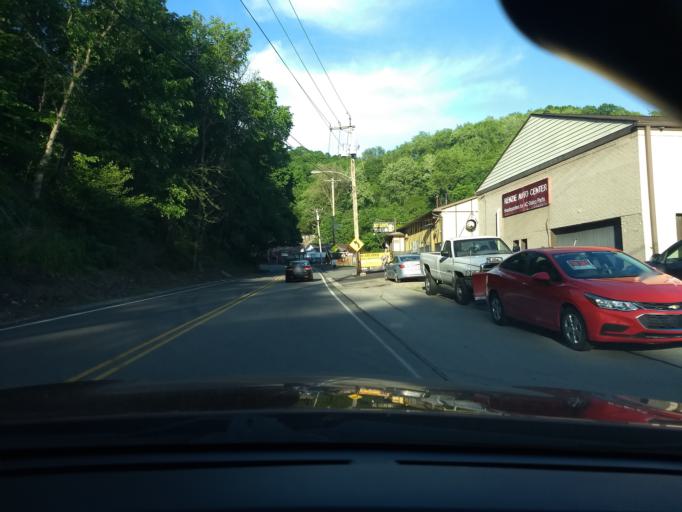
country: US
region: Pennsylvania
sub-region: Allegheny County
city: Versailles
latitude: 40.3281
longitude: -79.8367
